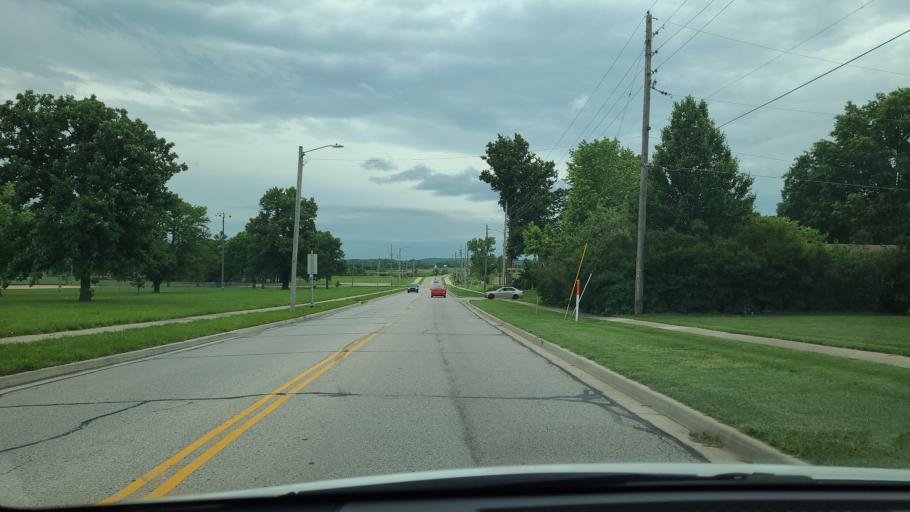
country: US
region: Kansas
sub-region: Douglas County
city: Lawrence
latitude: 38.9332
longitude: -95.2419
